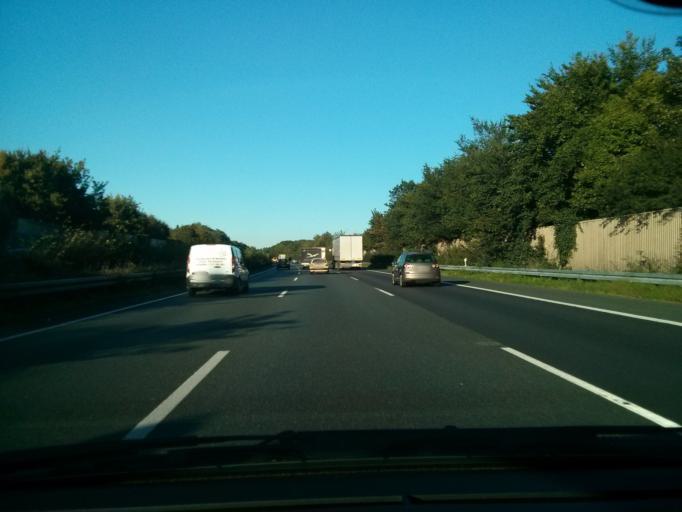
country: DE
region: North Rhine-Westphalia
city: Schwerte
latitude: 51.4711
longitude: 7.6001
